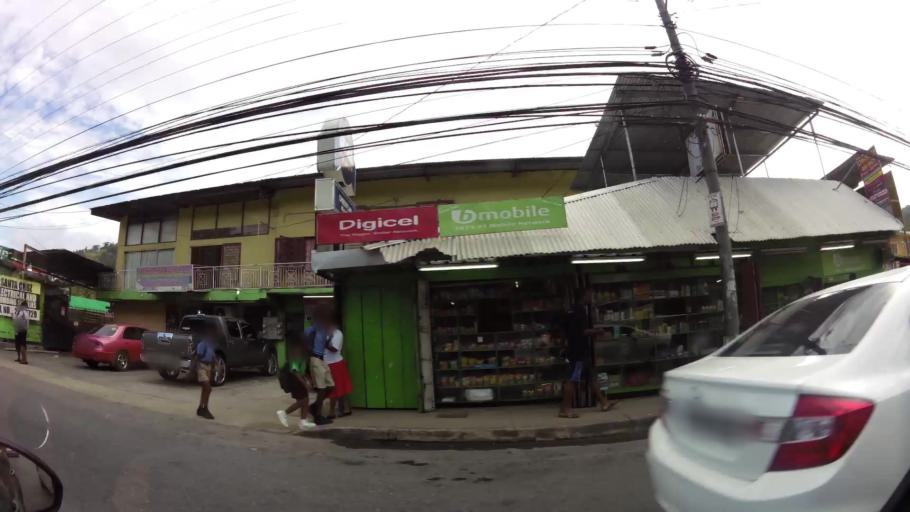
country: TT
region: San Juan/Laventille
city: Laventille
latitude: 10.6754
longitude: -61.4507
